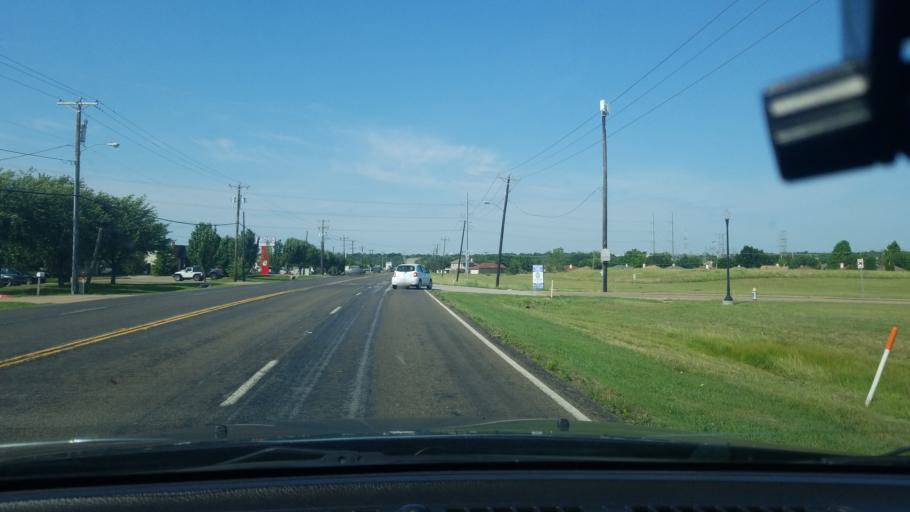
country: US
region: Texas
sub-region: Dallas County
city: Sunnyvale
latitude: 32.7773
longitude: -96.5682
